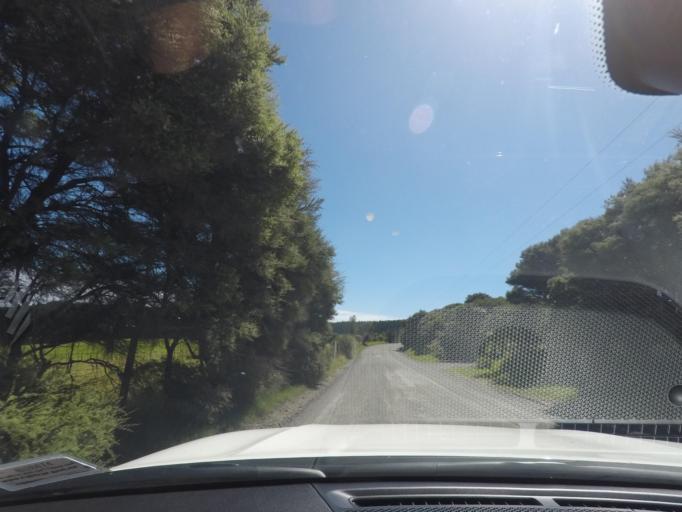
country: NZ
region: Auckland
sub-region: Auckland
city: Parakai
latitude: -36.5829
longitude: 174.3086
